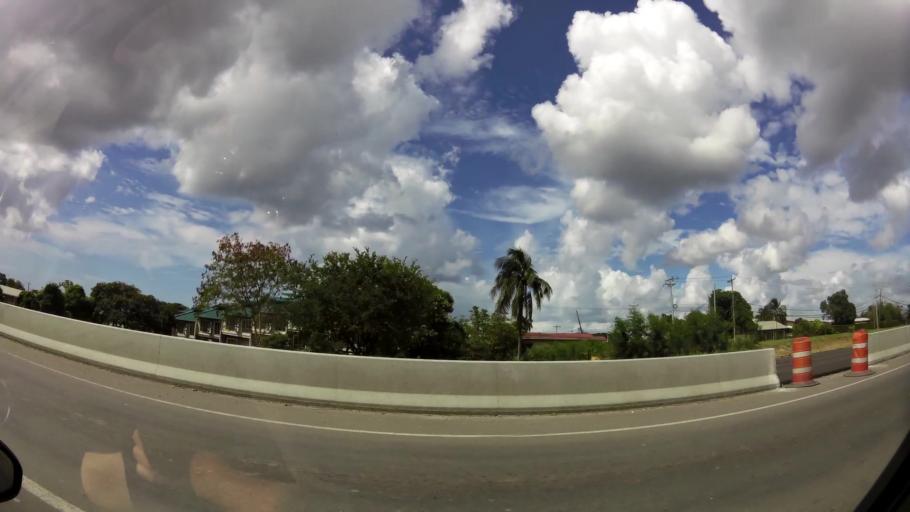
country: TT
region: City of San Fernando
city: San Fernando
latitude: 10.2517
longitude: -61.4843
